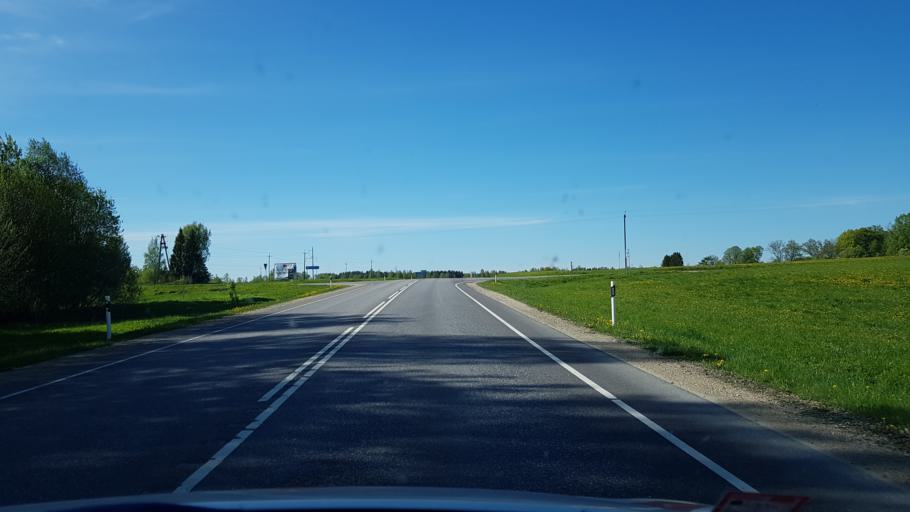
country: EE
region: Vorumaa
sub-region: Antsla vald
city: Vana-Antsla
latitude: 57.9861
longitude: 26.7683
